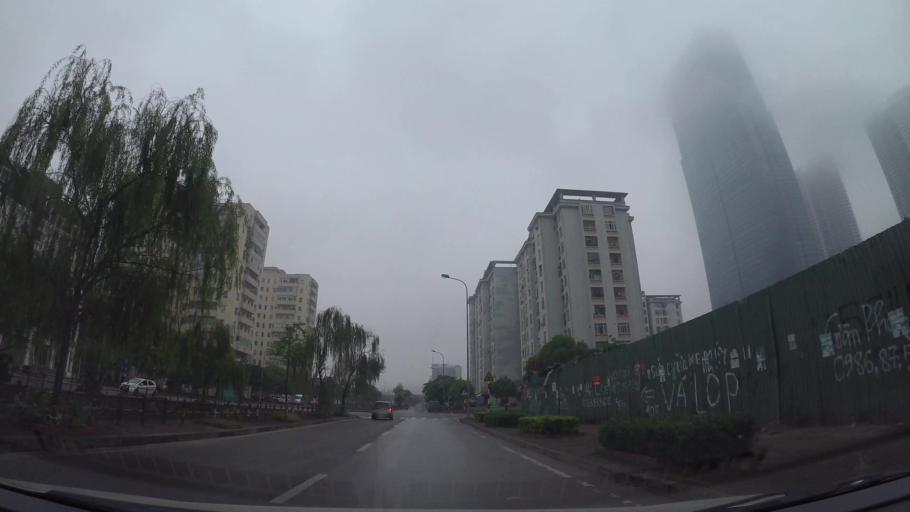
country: VN
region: Ha Noi
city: Cau Giay
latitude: 21.0162
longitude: 105.7879
